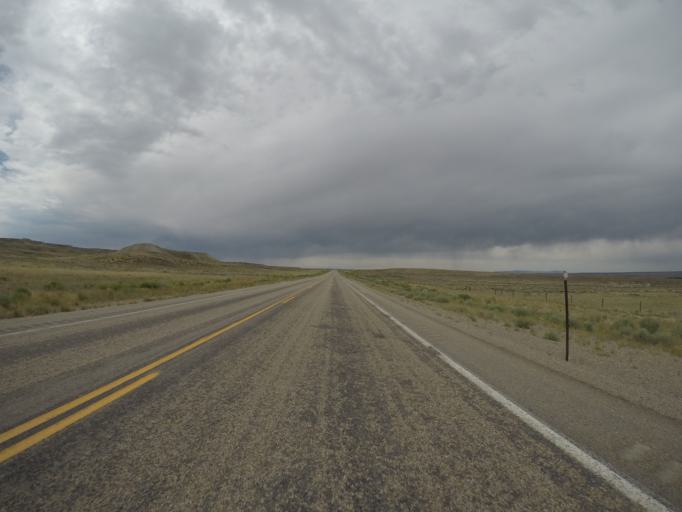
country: US
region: Wyoming
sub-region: Lincoln County
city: Kemmerer
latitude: 41.9523
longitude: -110.0253
